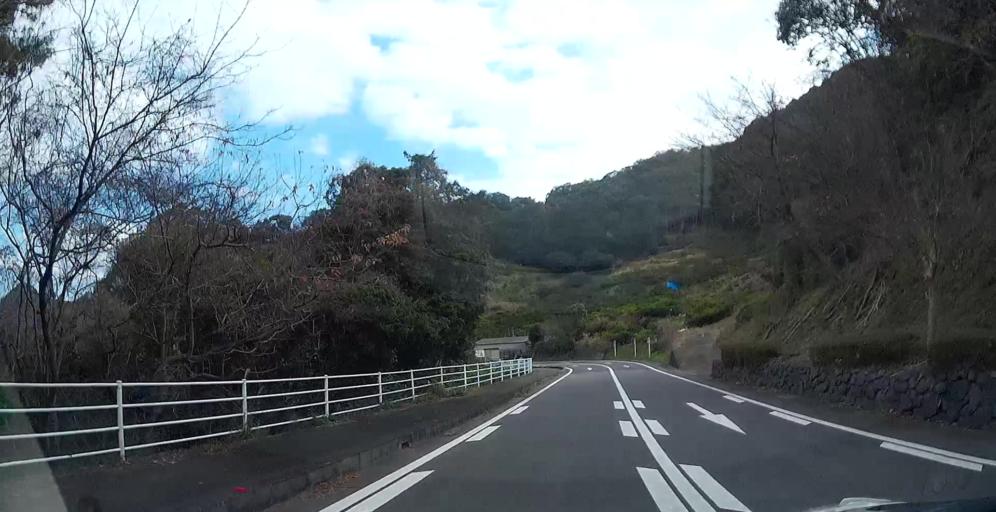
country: JP
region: Kumamoto
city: Minamata
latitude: 32.3270
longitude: 130.4752
